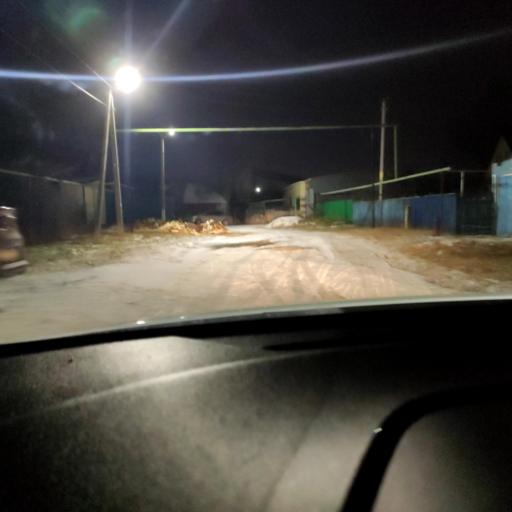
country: RU
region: Tatarstan
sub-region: Gorod Kazan'
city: Kazan
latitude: 55.7182
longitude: 49.0940
